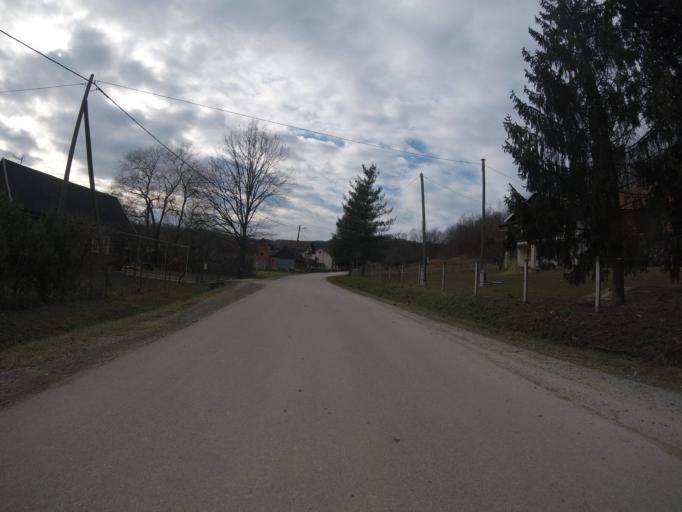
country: HR
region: Zagrebacka
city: Mraclin
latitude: 45.5053
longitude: 16.0460
